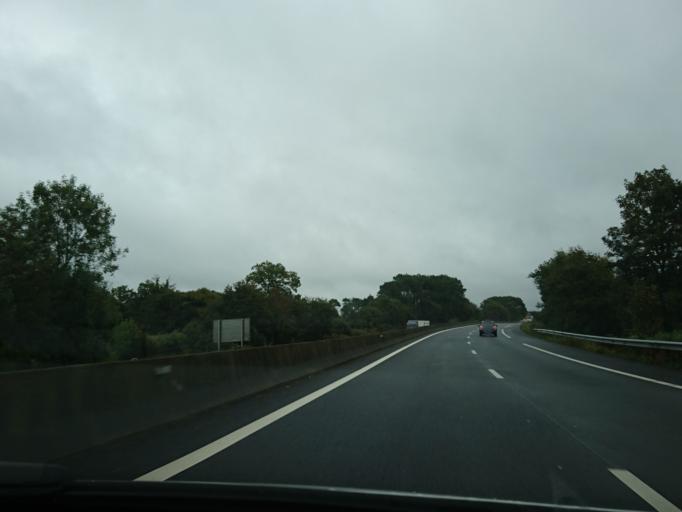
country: FR
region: Brittany
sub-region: Departement du Morbihan
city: Plougoumelen
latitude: 47.6723
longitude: -2.9315
